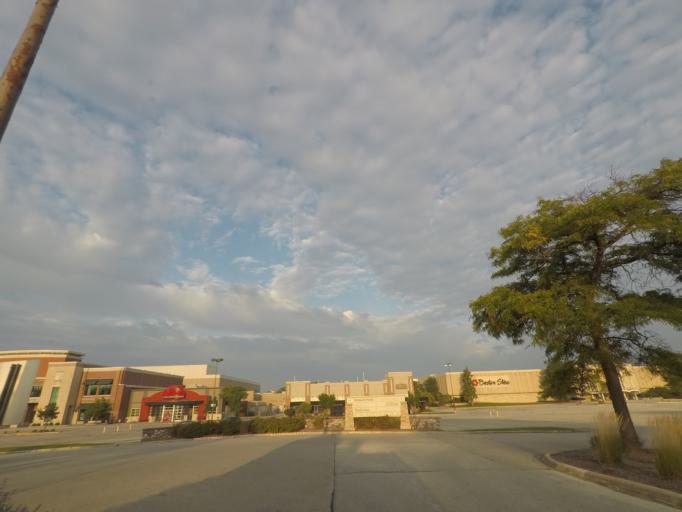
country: US
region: Wisconsin
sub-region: Waukesha County
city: Brookfield
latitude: 43.0334
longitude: -88.1073
